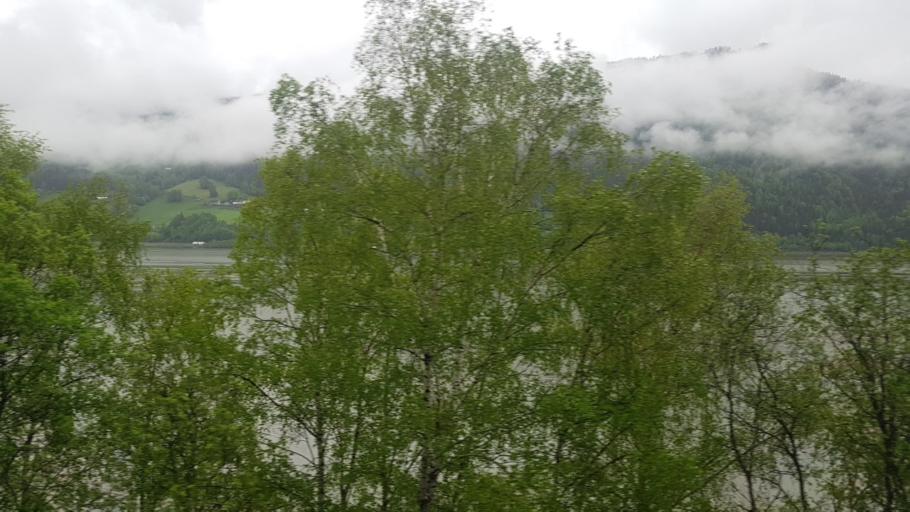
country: NO
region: Oppland
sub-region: Oyer
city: Tretten
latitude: 61.3426
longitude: 10.2854
